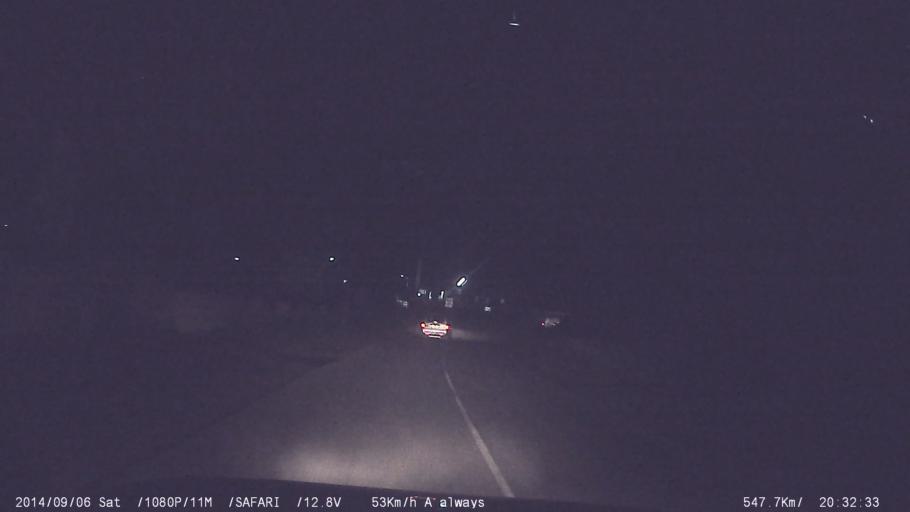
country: IN
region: Kerala
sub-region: Kottayam
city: Kottayam
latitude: 9.6622
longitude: 76.5514
